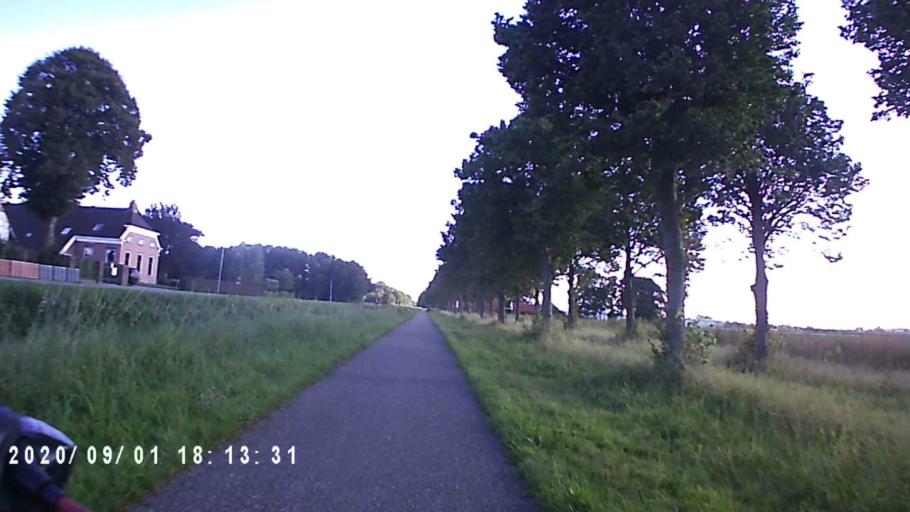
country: NL
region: Groningen
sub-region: Gemeente Hoogezand-Sappemeer
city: Sappemeer
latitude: 53.1832
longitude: 6.7861
